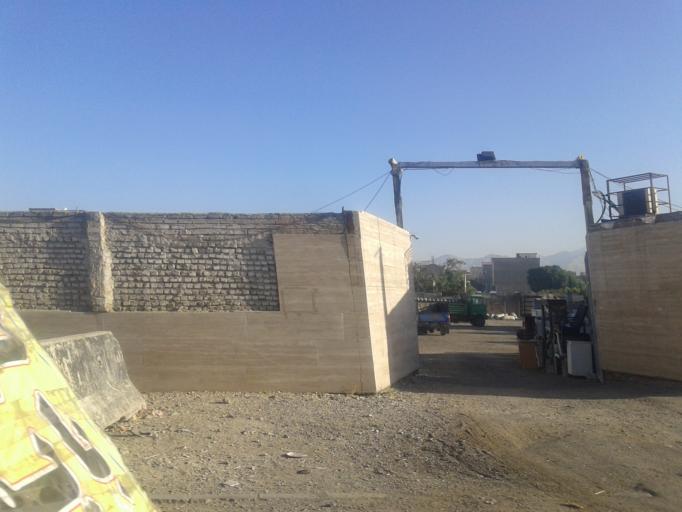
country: IR
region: Tehran
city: Rey
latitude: 35.6173
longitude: 51.3585
